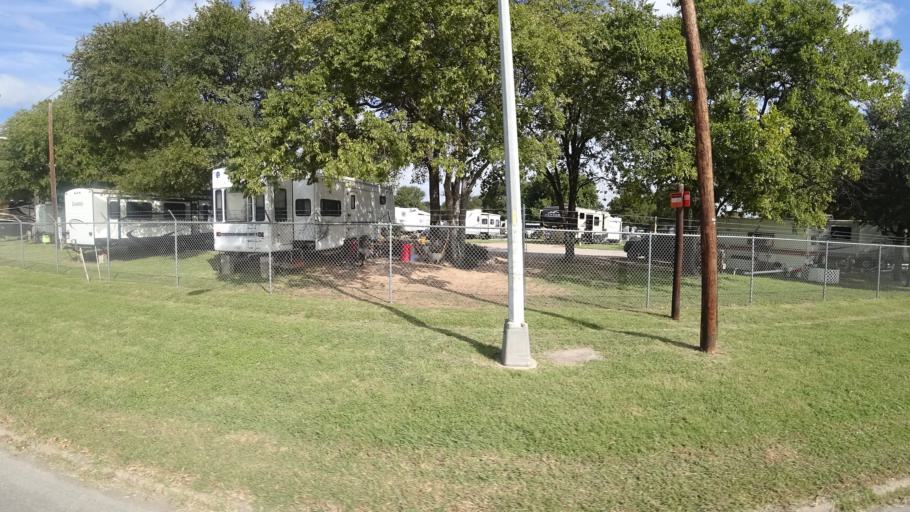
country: US
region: Texas
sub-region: Travis County
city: Austin
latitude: 30.2520
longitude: -97.6939
